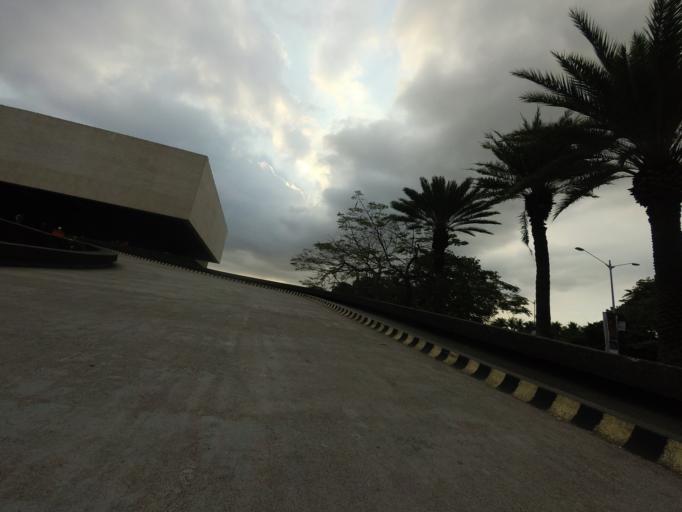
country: PH
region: Metro Manila
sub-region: City of Manila
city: Port Area
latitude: 14.5590
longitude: 120.9862
